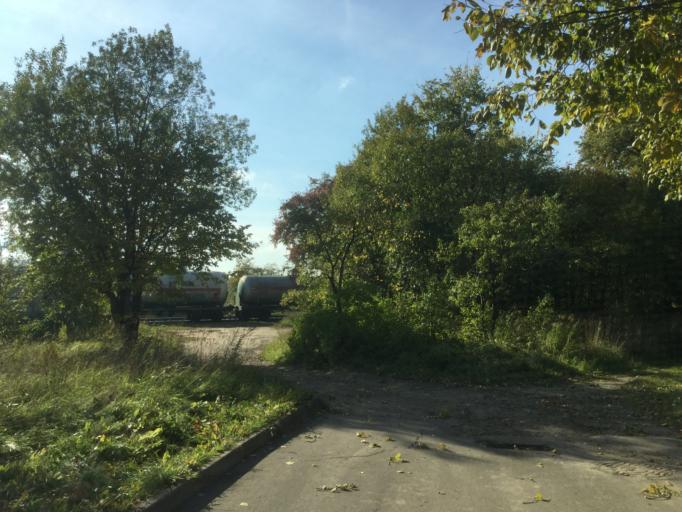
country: BY
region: Vitebsk
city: Vitebsk
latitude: 55.1716
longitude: 30.1930
